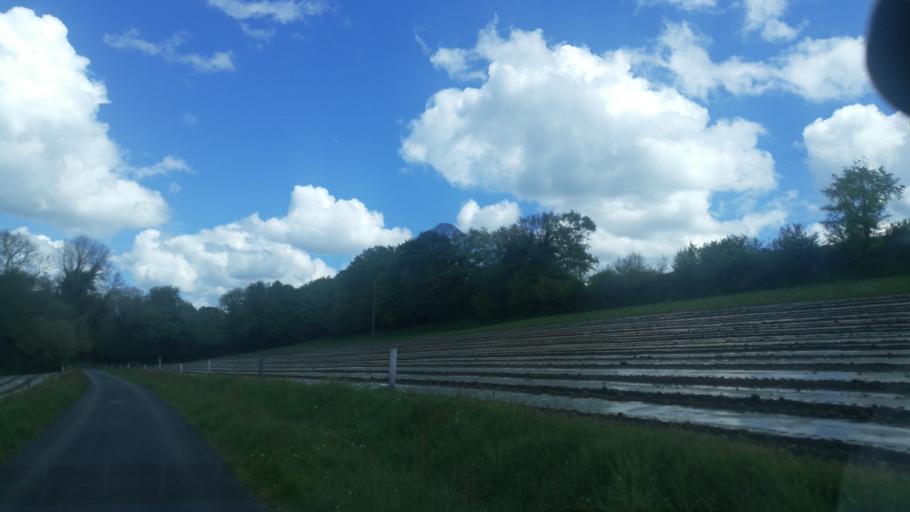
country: FR
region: Brittany
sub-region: Departement des Cotes-d'Armor
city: Saint-Nicolas-du-Pelem
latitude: 48.3169
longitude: -3.1346
